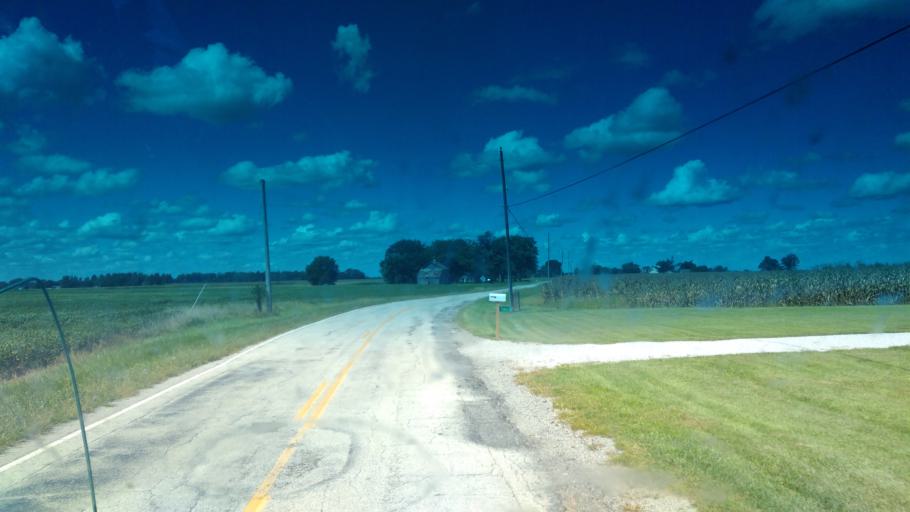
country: US
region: Ohio
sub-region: Madison County
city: West Jefferson
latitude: 40.0119
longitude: -83.3619
